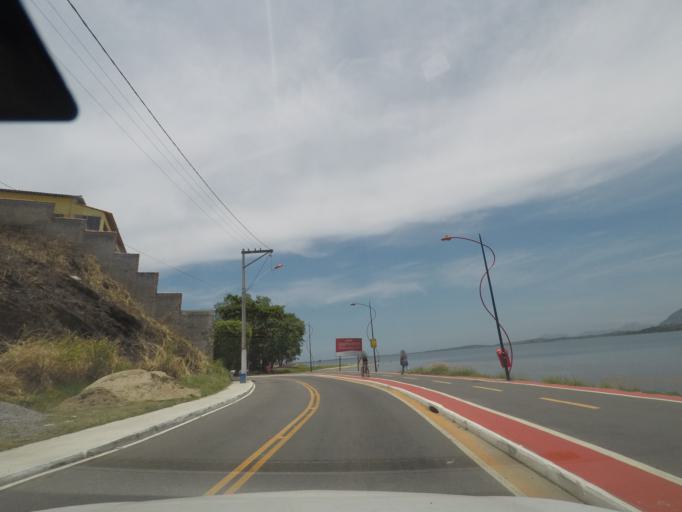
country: BR
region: Rio de Janeiro
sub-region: Marica
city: Marica
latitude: -22.9302
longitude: -42.8268
